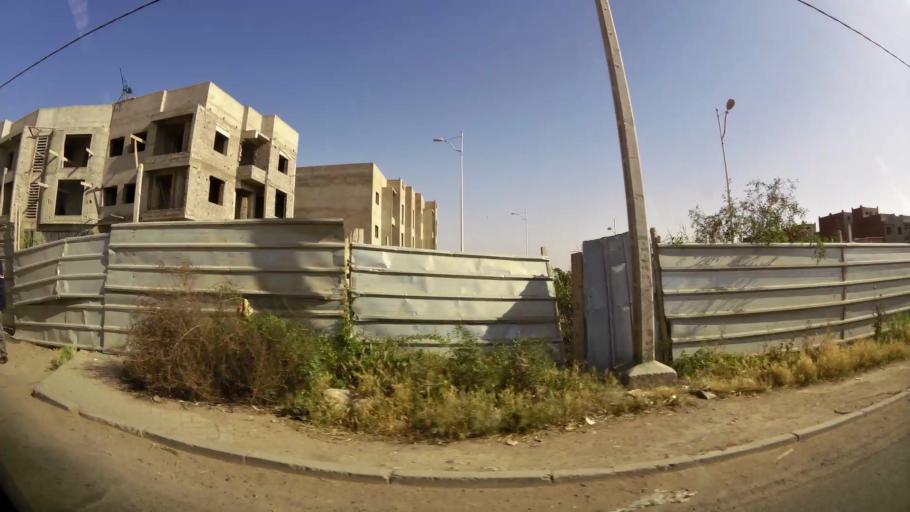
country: MA
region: Souss-Massa-Draa
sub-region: Inezgane-Ait Mellou
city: Inezgane
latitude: 30.3727
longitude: -9.5169
